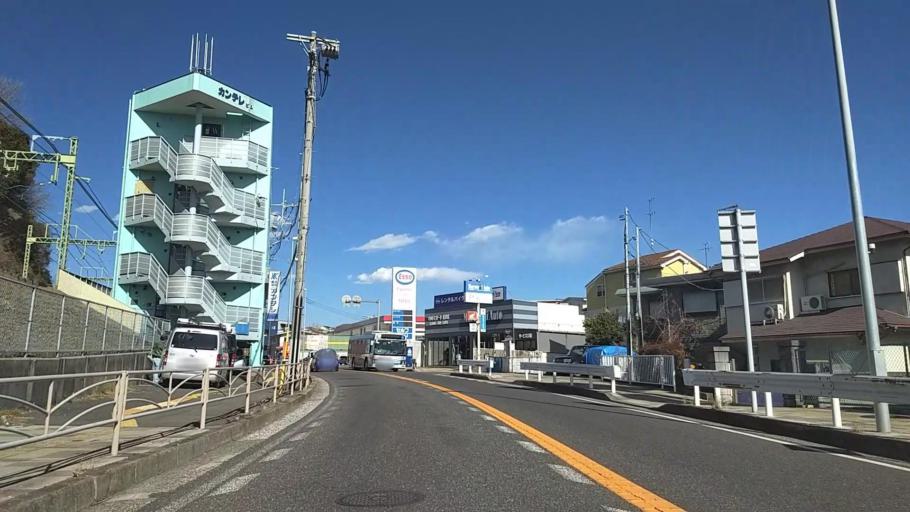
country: JP
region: Kanagawa
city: Zushi
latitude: 35.3510
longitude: 139.6268
